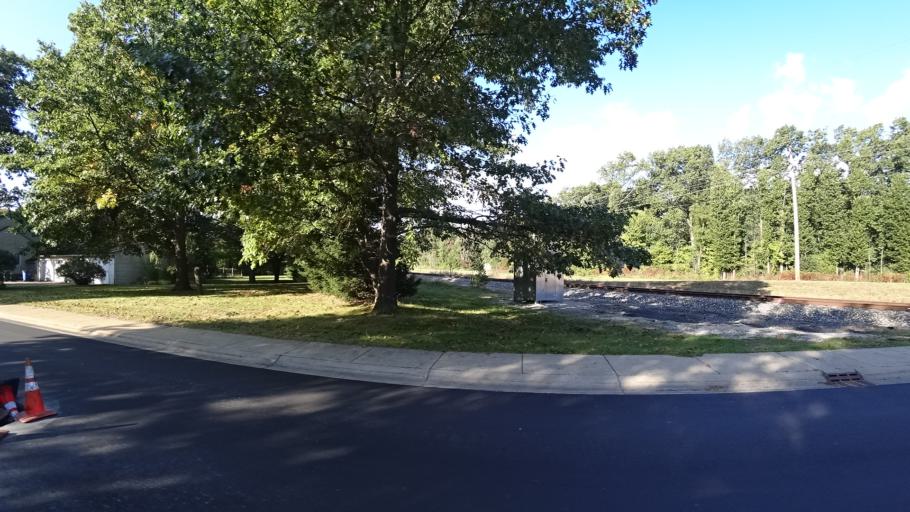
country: US
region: Indiana
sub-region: LaPorte County
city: Trail Creek
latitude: 41.7033
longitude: -86.8648
